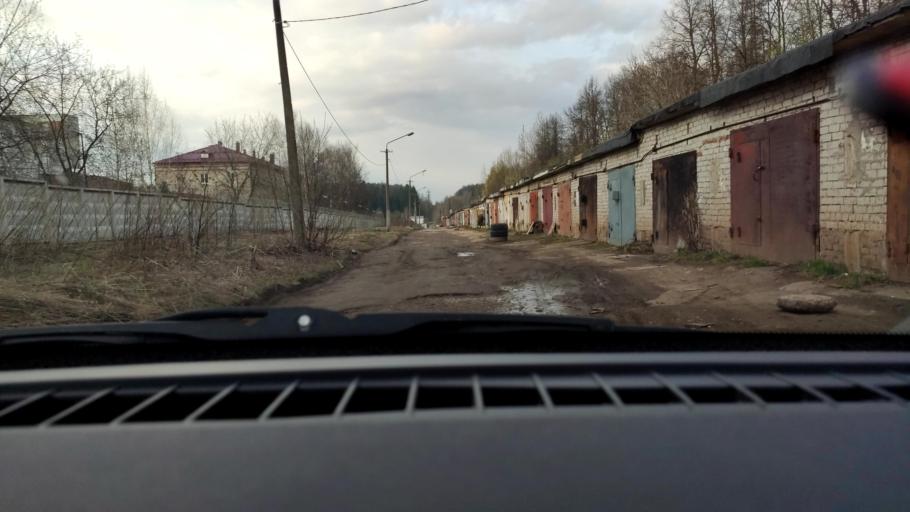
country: RU
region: Perm
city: Froly
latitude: 57.9732
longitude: 56.3214
